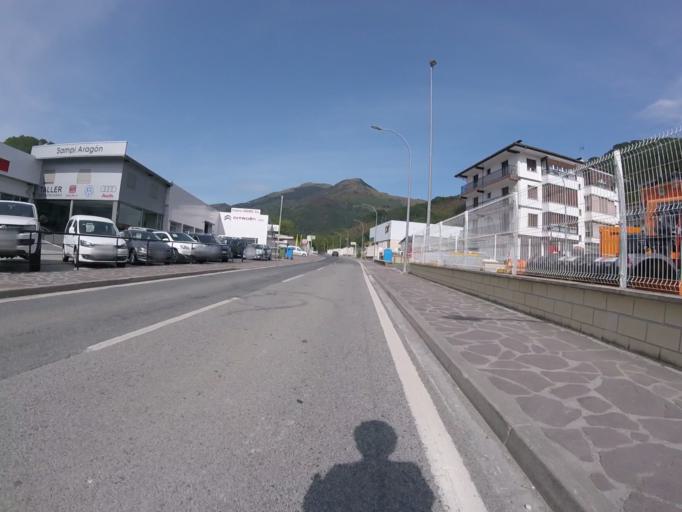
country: ES
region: Navarre
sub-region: Provincia de Navarra
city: Elgorriaga
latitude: 43.1355
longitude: -1.6790
